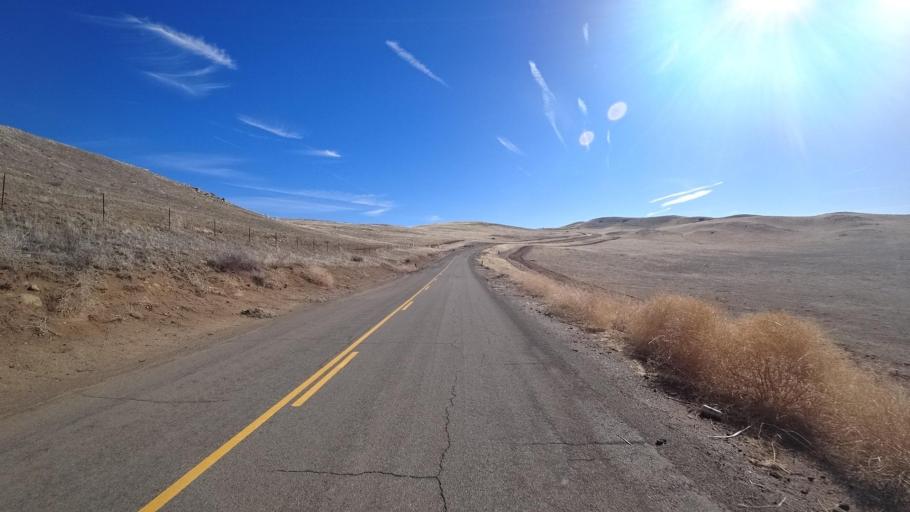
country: US
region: California
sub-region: Kern County
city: Maricopa
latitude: 34.9114
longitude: -119.3963
